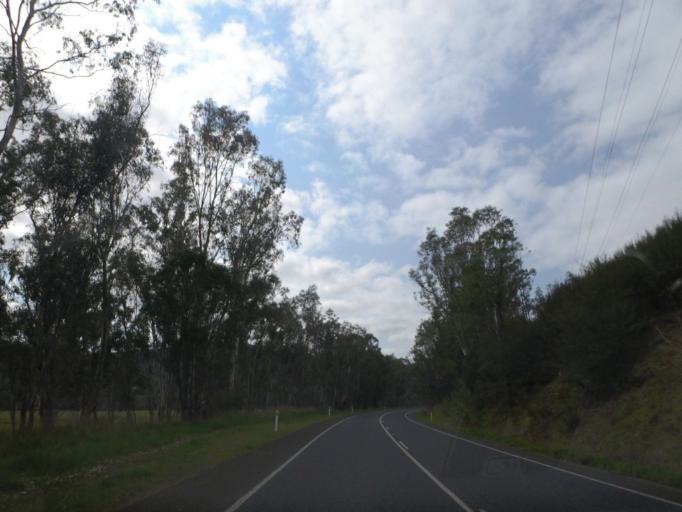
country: AU
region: Victoria
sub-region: Murrindindi
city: Kinglake West
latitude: -37.1415
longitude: 145.2589
